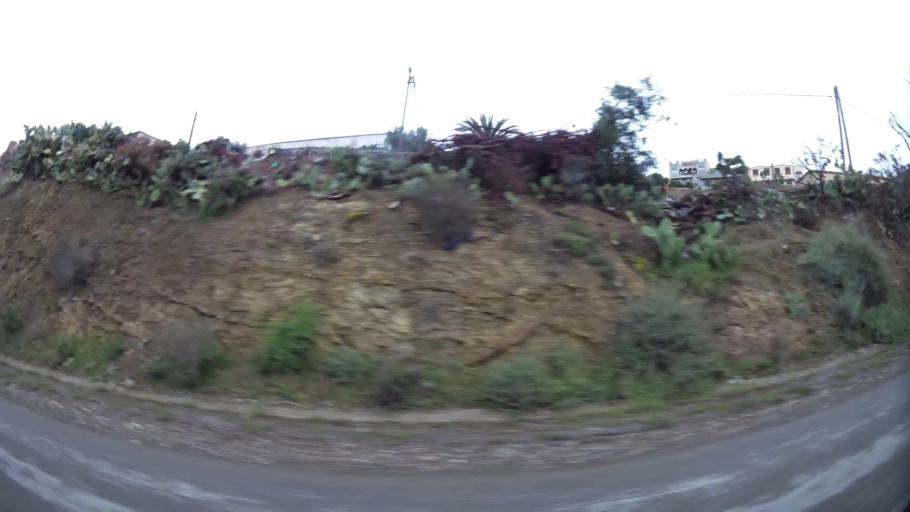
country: MA
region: Taza-Al Hoceima-Taounate
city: Imzourene
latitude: 34.9515
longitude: -3.8078
